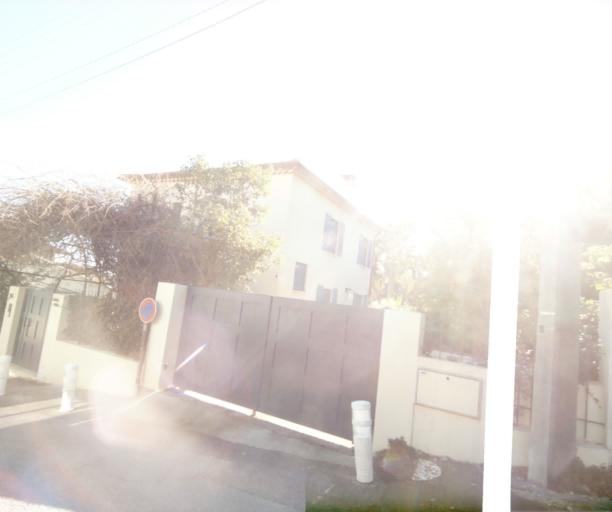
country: FR
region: Provence-Alpes-Cote d'Azur
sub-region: Departement des Alpes-Maritimes
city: Antibes
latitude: 43.5754
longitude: 7.1187
